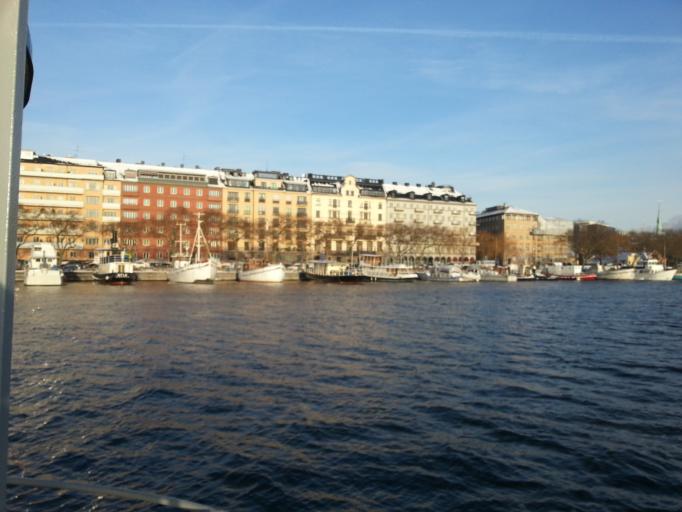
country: SE
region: Stockholm
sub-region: Stockholms Kommun
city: Stockholm
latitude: 59.3255
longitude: 18.0468
